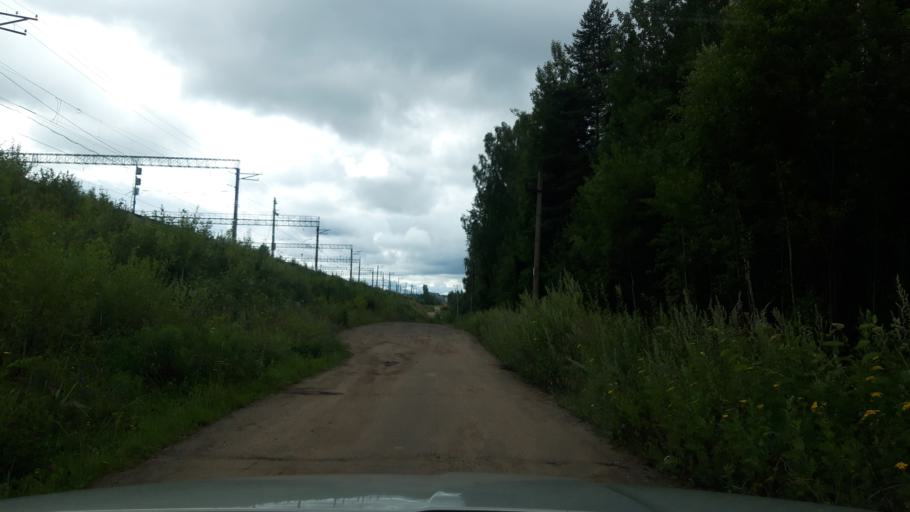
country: RU
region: Moskovskaya
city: Povarovo
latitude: 56.0532
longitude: 37.0576
